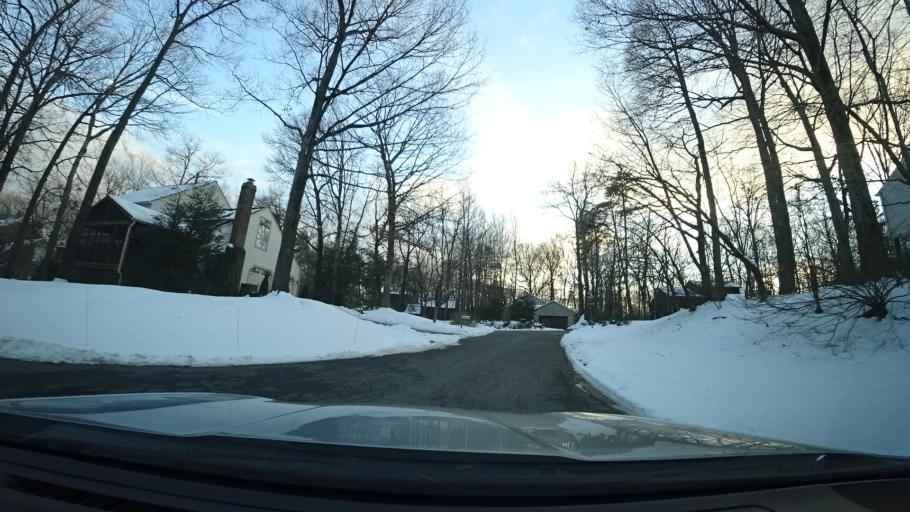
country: US
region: Virginia
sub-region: Fairfax County
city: Reston
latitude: 38.9748
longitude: -77.3460
